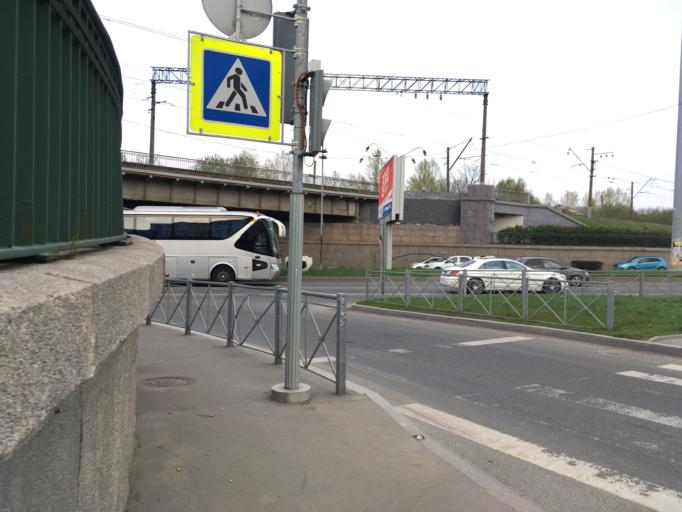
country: RU
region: St.-Petersburg
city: Centralniy
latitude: 59.9022
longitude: 30.3395
